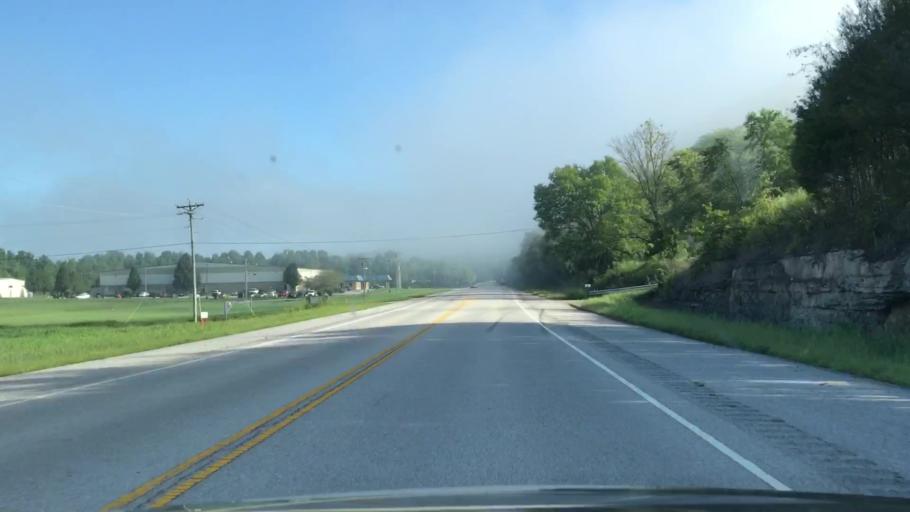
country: US
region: Tennessee
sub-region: Jackson County
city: Gainesboro
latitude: 36.3907
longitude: -85.6359
